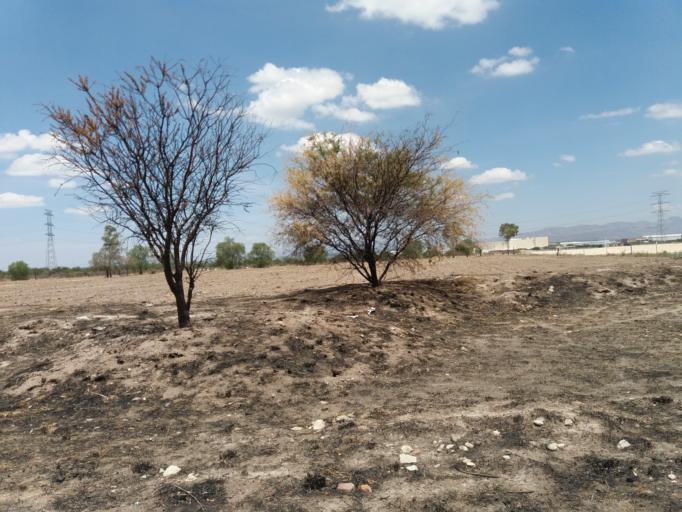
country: MX
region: Aguascalientes
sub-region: Aguascalientes
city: San Sebastian [Fraccionamiento]
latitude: 21.7922
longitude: -102.2825
